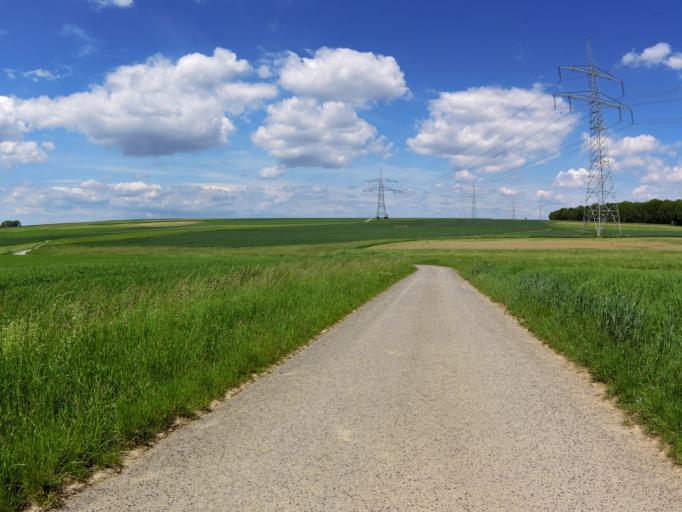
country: DE
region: Bavaria
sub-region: Regierungsbezirk Unterfranken
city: Theilheim
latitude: 49.7243
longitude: 10.0497
